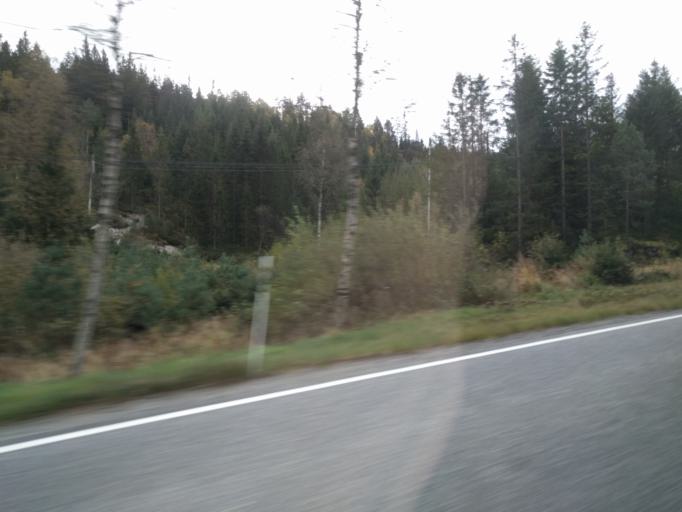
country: NO
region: Vest-Agder
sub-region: Songdalen
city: Nodeland
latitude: 58.3224
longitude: 7.8085
